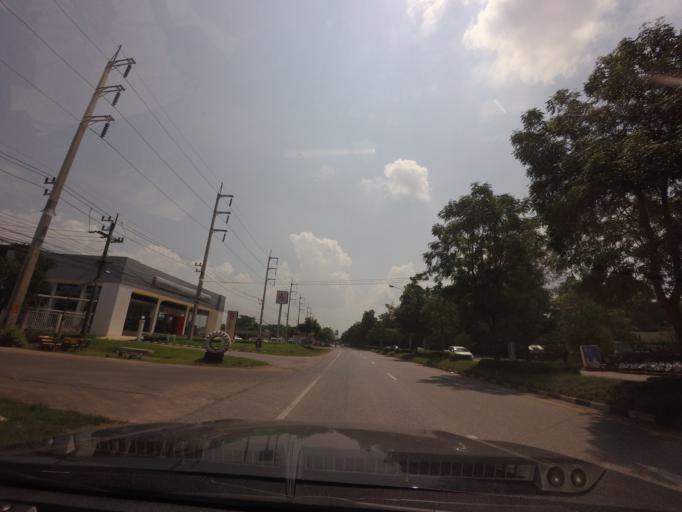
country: TH
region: Uttaradit
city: Uttaradit
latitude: 17.6012
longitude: 100.1248
